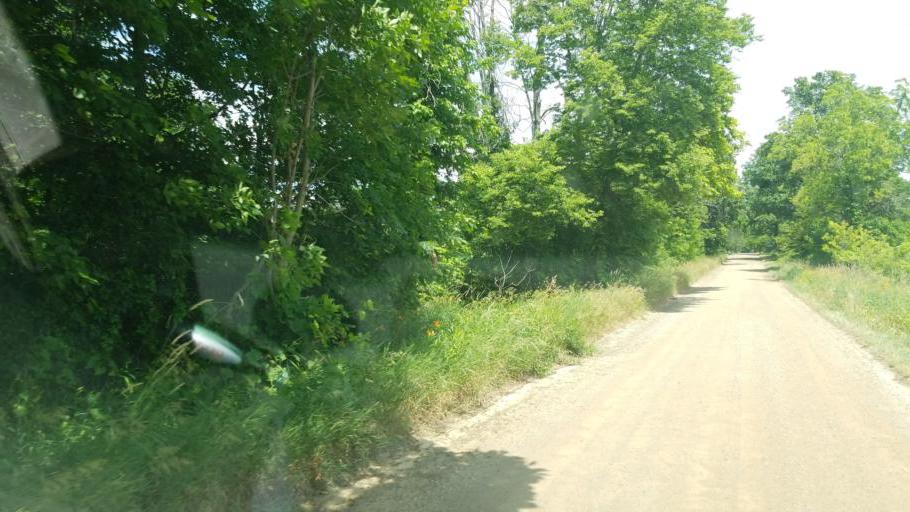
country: US
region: Michigan
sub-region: Eaton County
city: Charlotte
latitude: 42.6162
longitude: -84.8854
